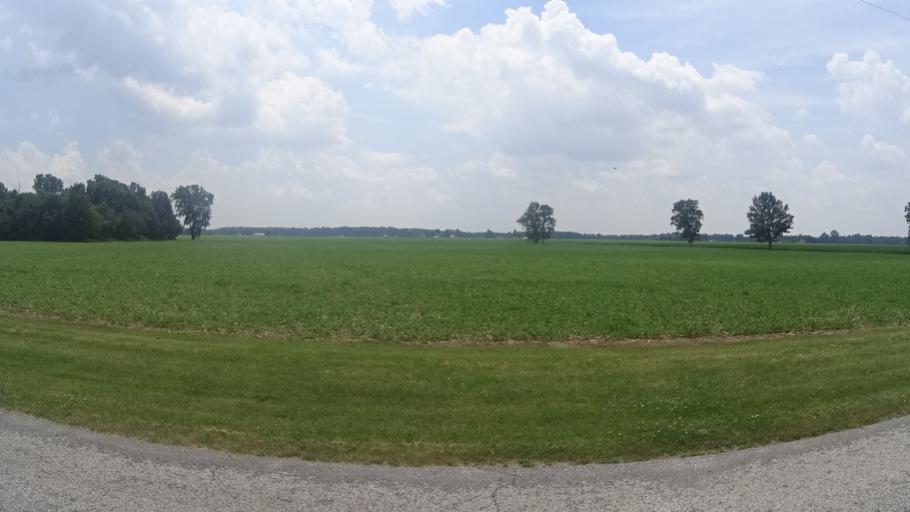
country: US
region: Ohio
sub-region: Erie County
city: Milan
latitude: 41.3111
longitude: -82.6456
